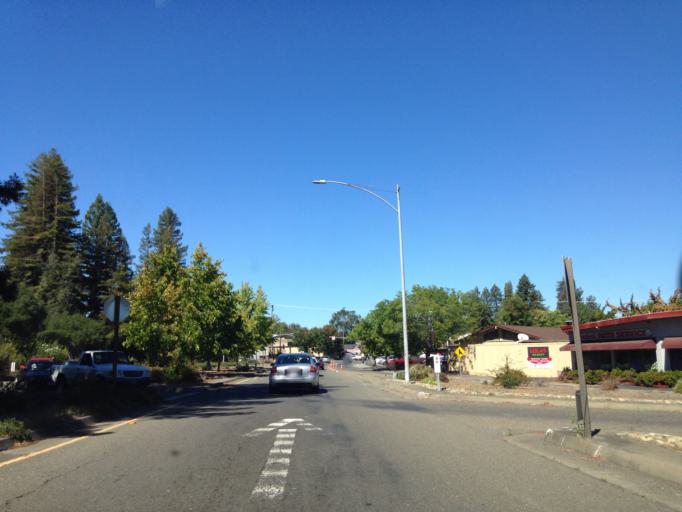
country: US
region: California
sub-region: Sonoma County
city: Healdsburg
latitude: 38.6037
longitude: -122.8673
